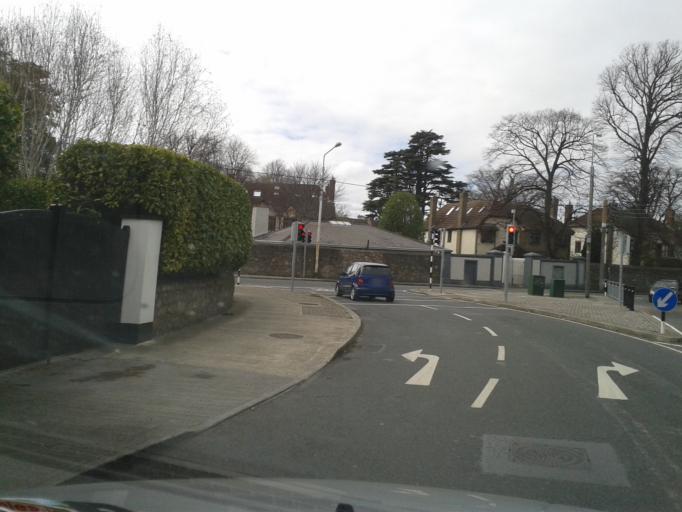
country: IE
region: Leinster
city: Monkstown
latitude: 53.2906
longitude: -6.1661
